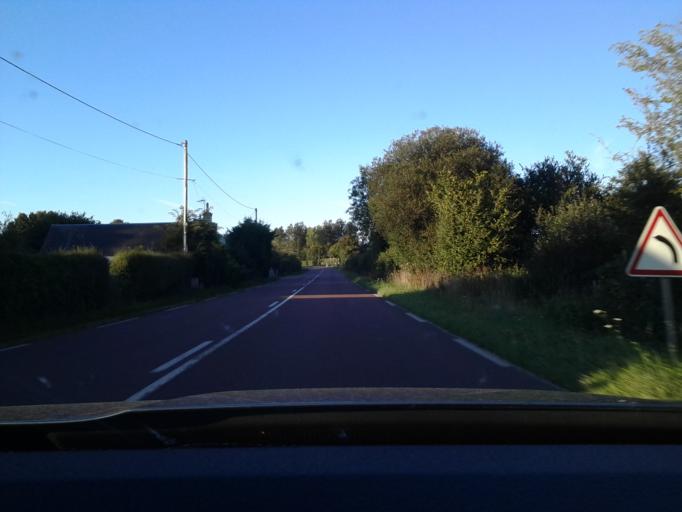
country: FR
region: Lower Normandy
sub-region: Departement de la Manche
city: Saint-Sauveur-le-Vicomte
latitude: 49.4226
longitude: -1.4958
